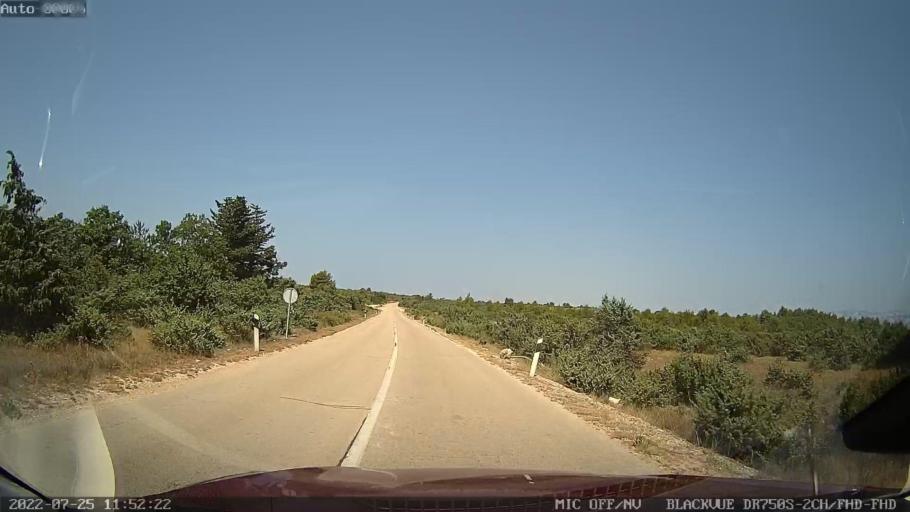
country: HR
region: Zadarska
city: Vrsi
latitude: 44.2474
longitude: 15.2450
